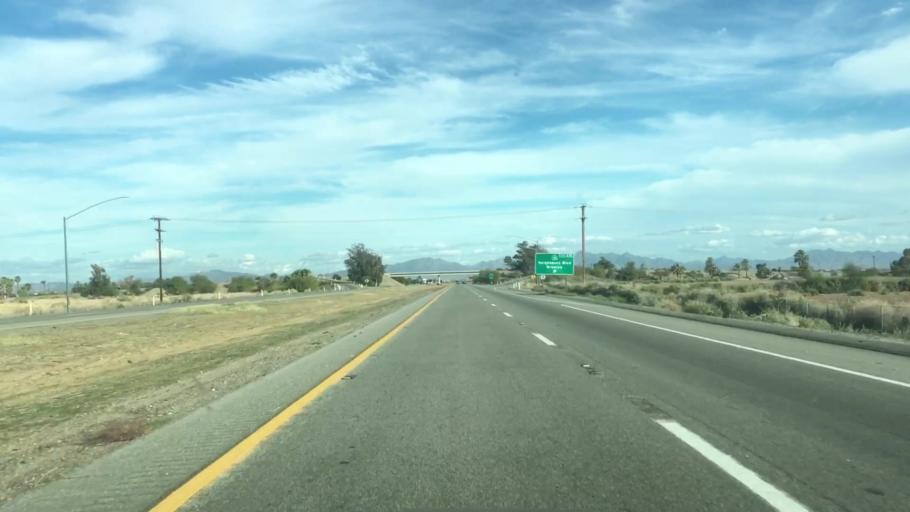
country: US
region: California
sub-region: Riverside County
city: Blythe
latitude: 33.6065
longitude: -114.6633
